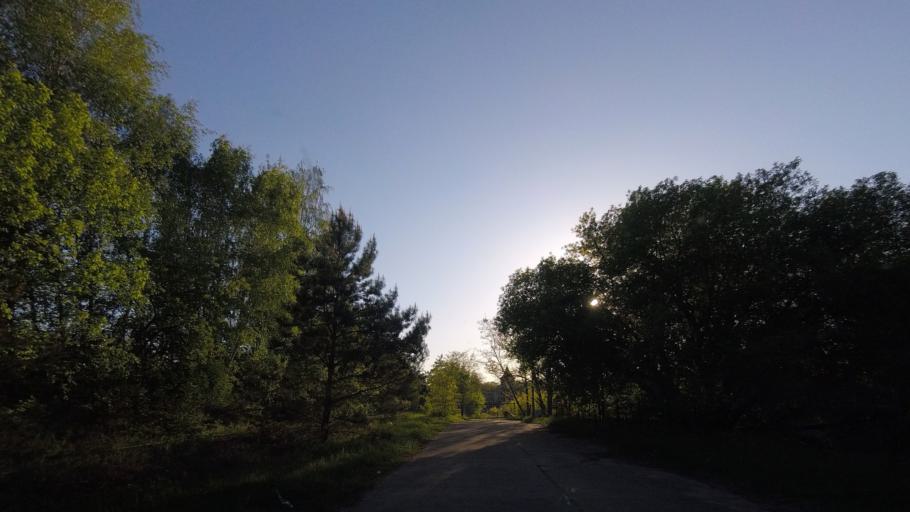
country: DE
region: Brandenburg
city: Juterbog
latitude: 52.0062
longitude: 13.0716
